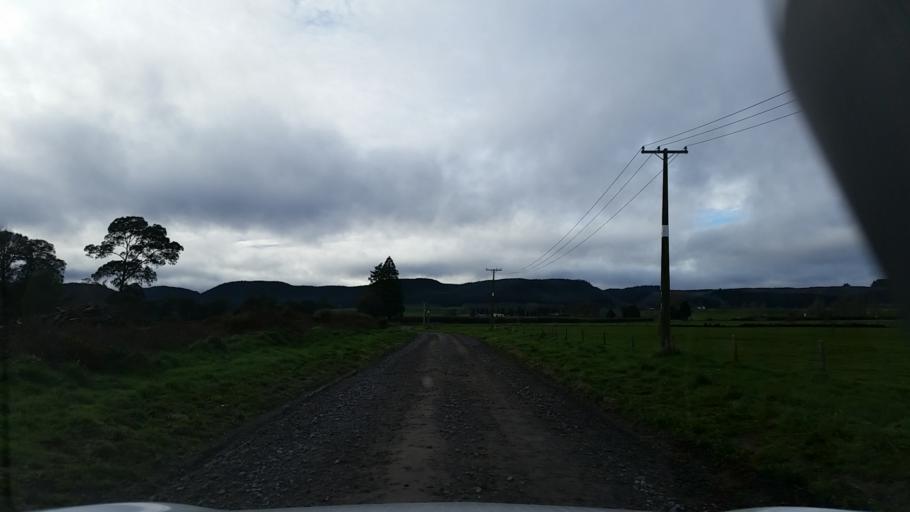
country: NZ
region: Bay of Plenty
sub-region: Rotorua District
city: Rotorua
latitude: -38.4061
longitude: 176.3687
